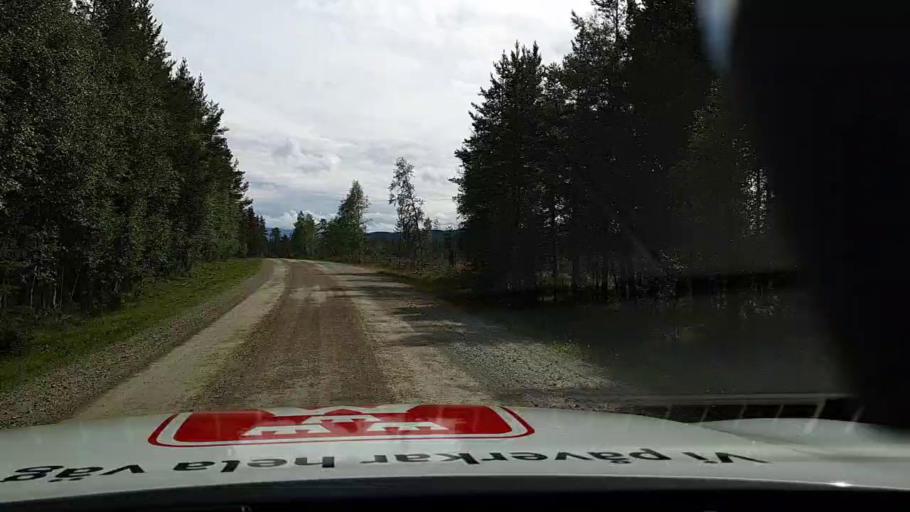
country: SE
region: Jaemtland
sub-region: Are Kommun
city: Jarpen
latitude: 62.5202
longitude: 13.4877
